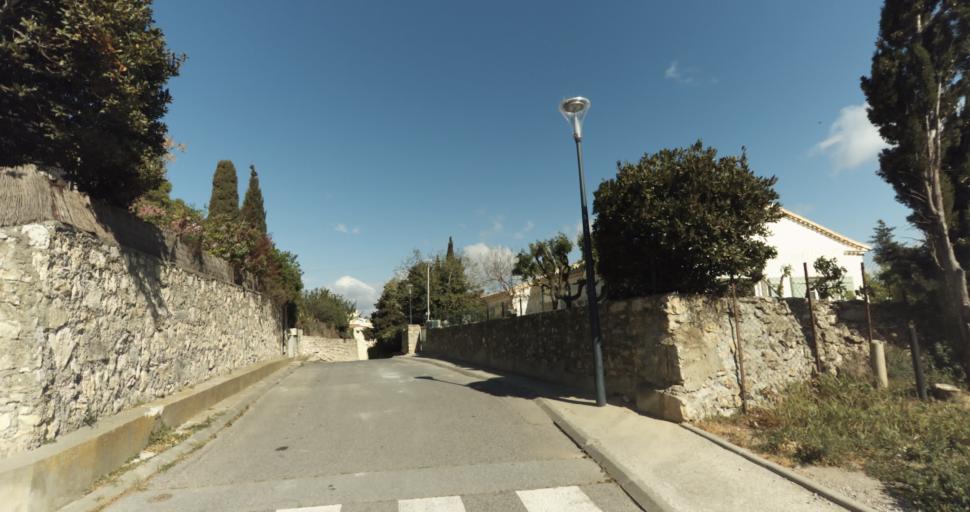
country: FR
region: Languedoc-Roussillon
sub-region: Departement de l'Aude
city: Leucate
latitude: 42.9094
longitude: 3.0315
